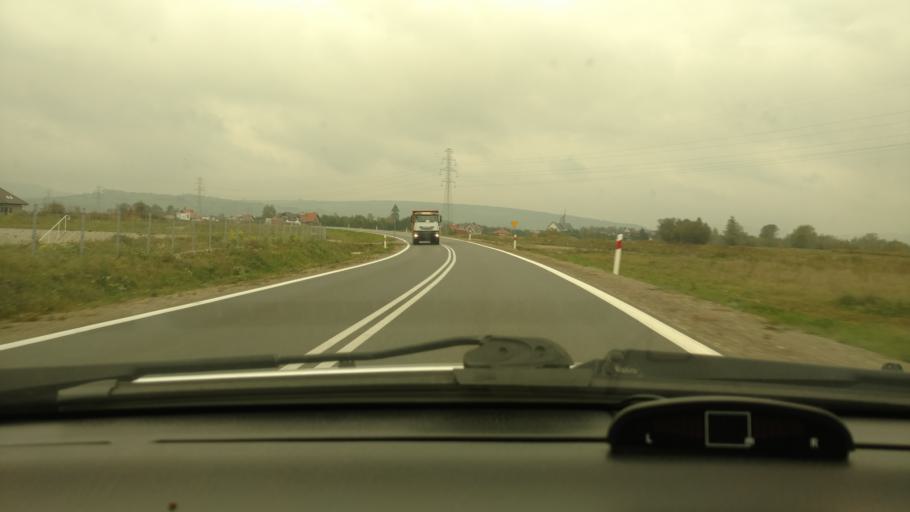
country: PL
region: Lesser Poland Voivodeship
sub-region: Powiat nowosadecki
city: Stary Sacz
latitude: 49.5957
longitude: 20.6481
